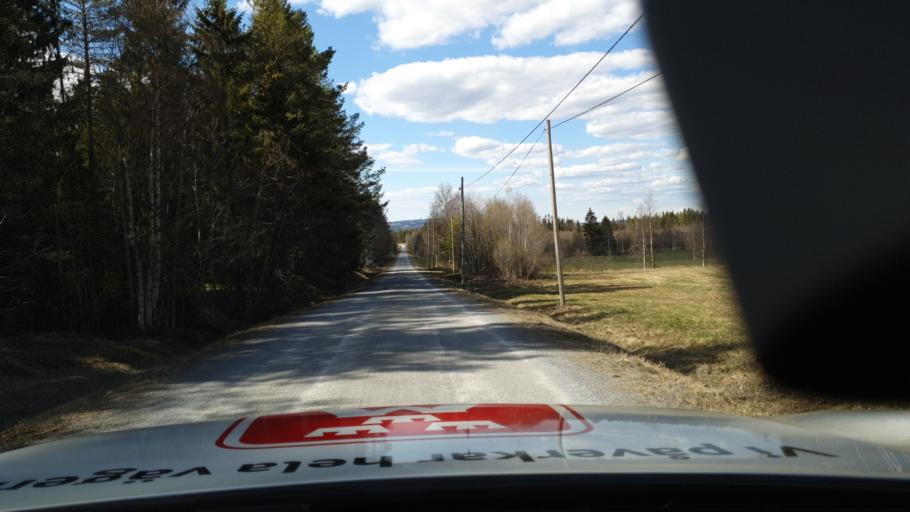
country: SE
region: Jaemtland
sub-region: Bergs Kommun
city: Hoverberg
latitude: 62.8412
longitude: 14.4392
